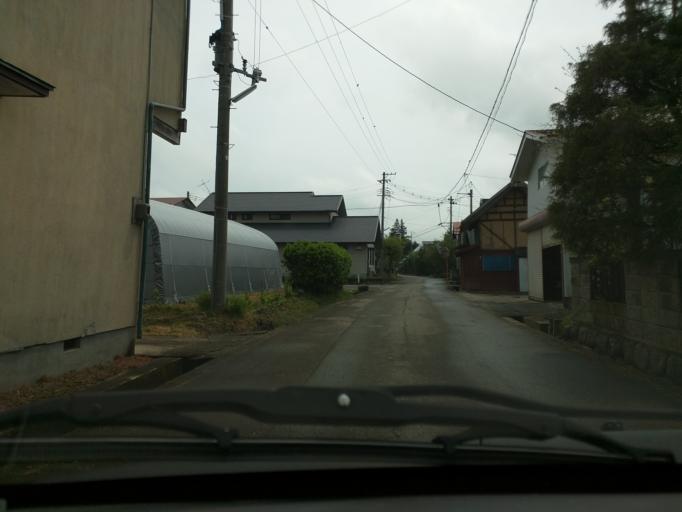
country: JP
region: Fukushima
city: Kitakata
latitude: 37.4437
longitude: 139.8804
